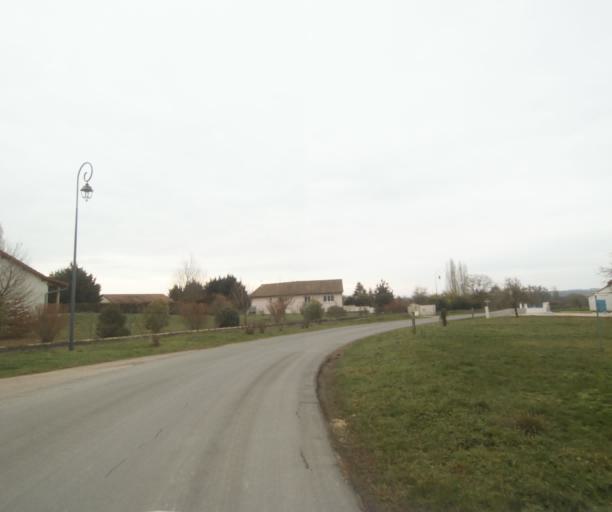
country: FR
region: Champagne-Ardenne
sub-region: Departement de la Haute-Marne
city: Villiers-en-Lieu
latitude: 48.6367
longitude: 4.7702
